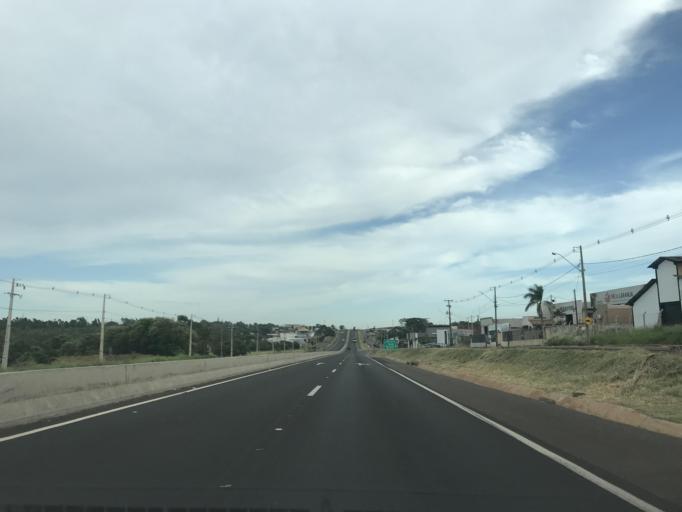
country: BR
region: Parana
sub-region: Alto Parana
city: Alto Parana
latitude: -23.1333
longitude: -52.2960
